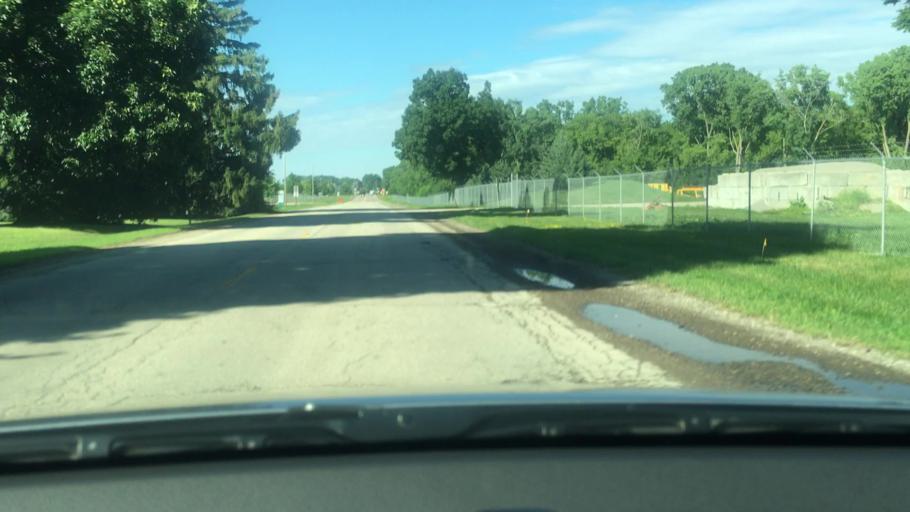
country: US
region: Wisconsin
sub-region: Winnebago County
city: Oshkosh
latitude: 43.9859
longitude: -88.5486
